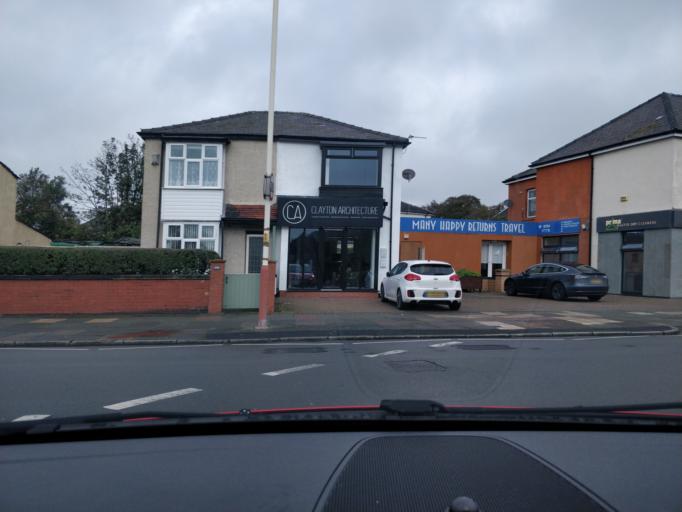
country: GB
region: England
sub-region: Sefton
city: Southport
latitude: 53.6030
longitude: -3.0337
